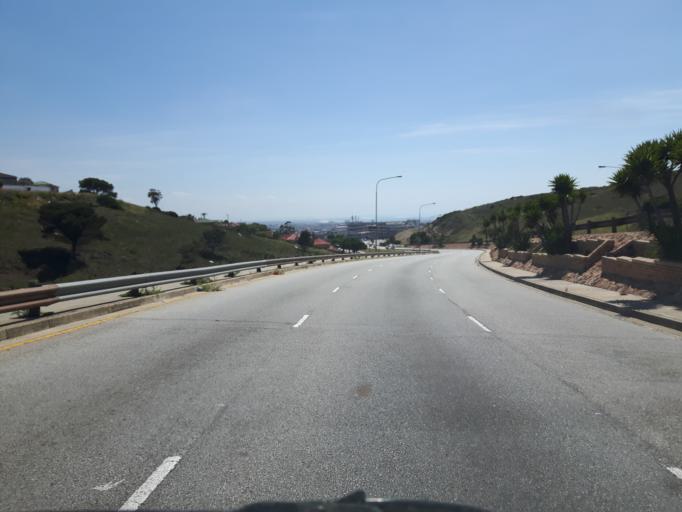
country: ZA
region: Eastern Cape
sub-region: Nelson Mandela Bay Metropolitan Municipality
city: Port Elizabeth
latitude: -33.9416
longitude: 25.5777
